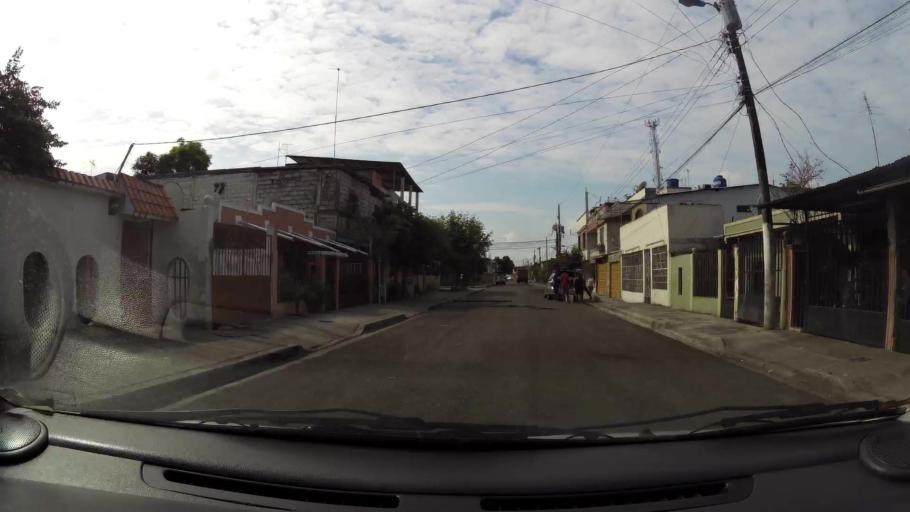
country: EC
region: Guayas
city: Guayaquil
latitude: -2.2598
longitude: -79.8936
